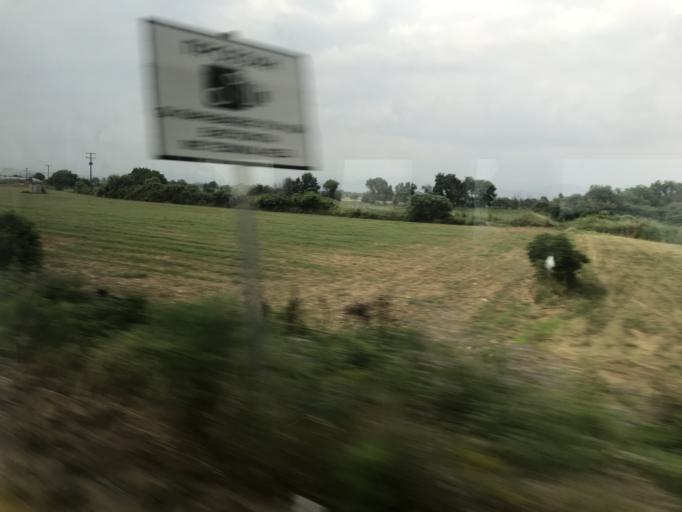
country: GR
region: East Macedonia and Thrace
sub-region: Nomos Rodopis
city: Arisvi
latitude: 41.0482
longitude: 25.6285
